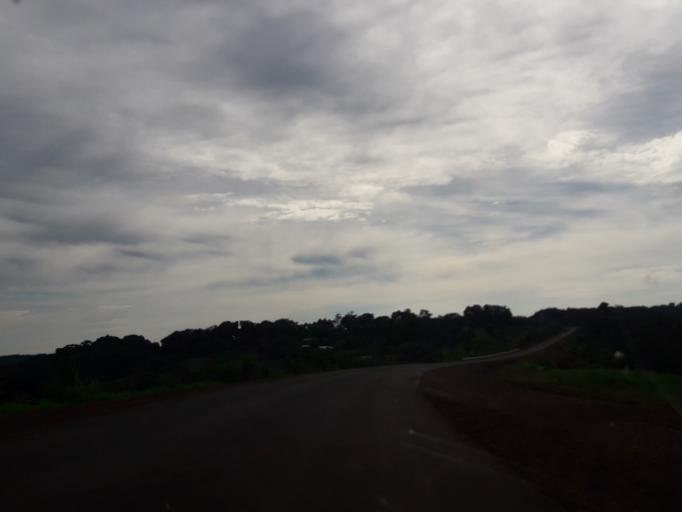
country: AR
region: Misiones
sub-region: Departamento de San Pedro
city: San Pedro
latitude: -26.5083
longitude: -53.9196
